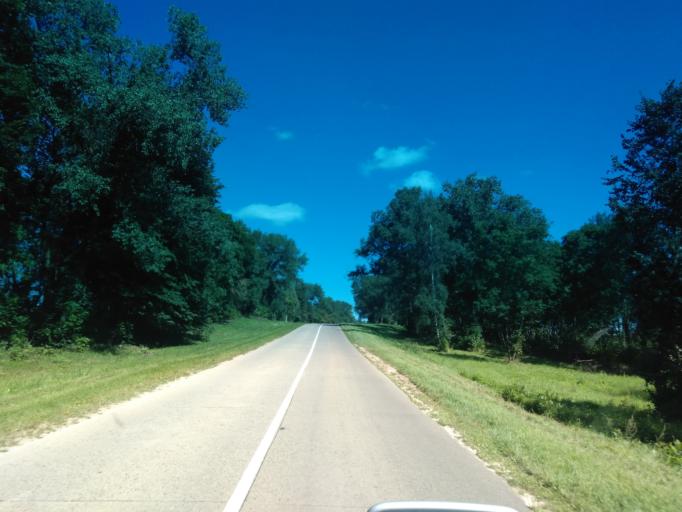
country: BY
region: Minsk
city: Stan'kava
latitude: 53.6420
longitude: 27.2919
